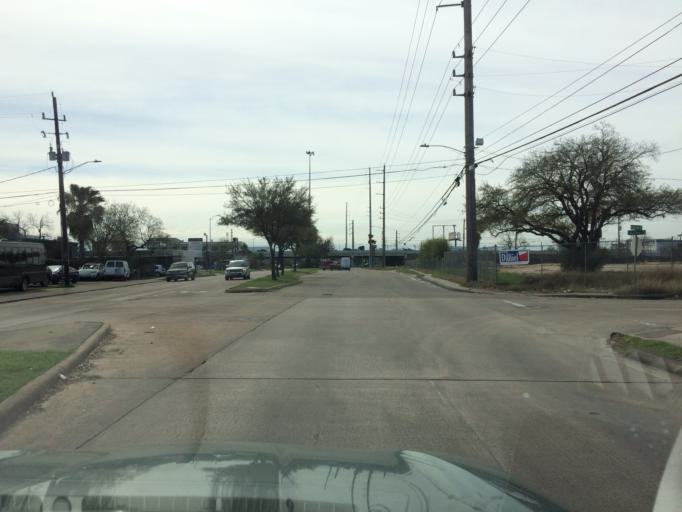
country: US
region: Texas
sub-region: Harris County
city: Bellaire
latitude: 29.7286
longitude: -95.4842
